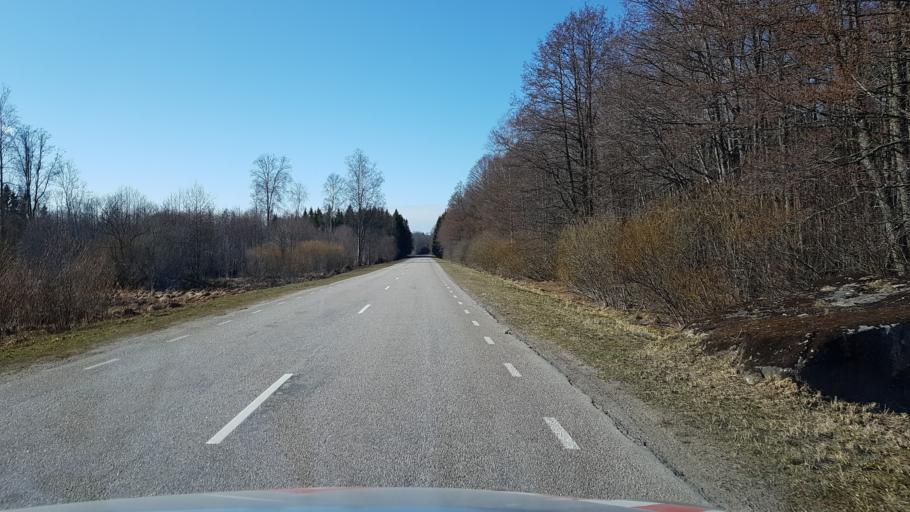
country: EE
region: Laeaene-Virumaa
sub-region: Haljala vald
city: Haljala
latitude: 59.5161
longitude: 26.0944
